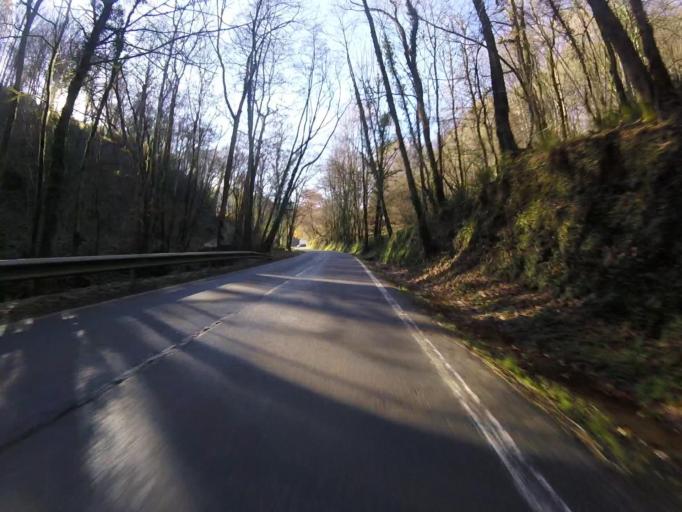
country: ES
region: Navarre
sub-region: Provincia de Navarra
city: Bera
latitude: 43.2821
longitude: -1.6511
